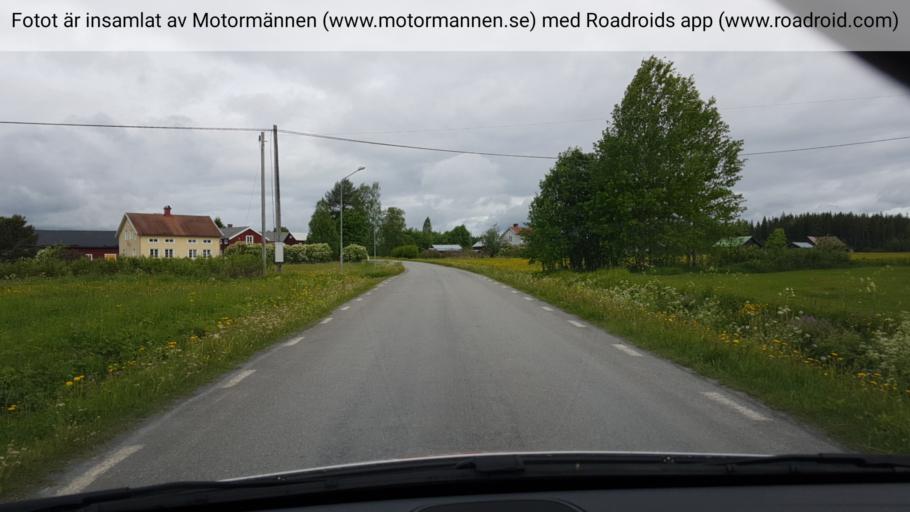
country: SE
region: Jaemtland
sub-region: OEstersunds Kommun
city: Lit
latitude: 63.2732
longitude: 14.9431
